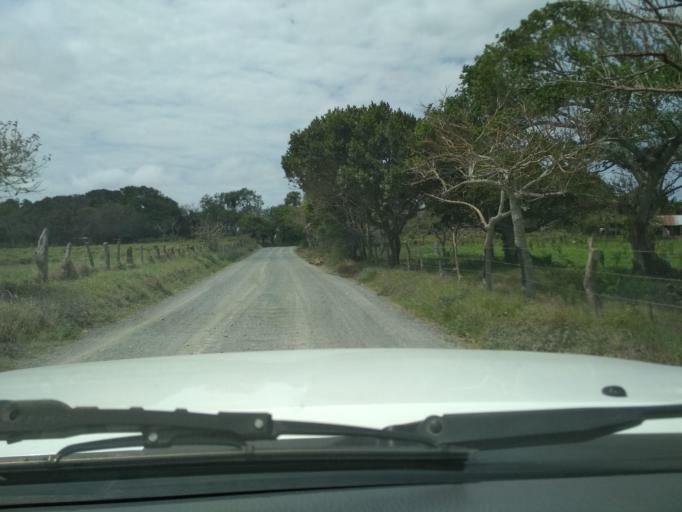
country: MX
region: Veracruz
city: Anton Lizardo
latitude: 19.0081
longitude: -95.9844
